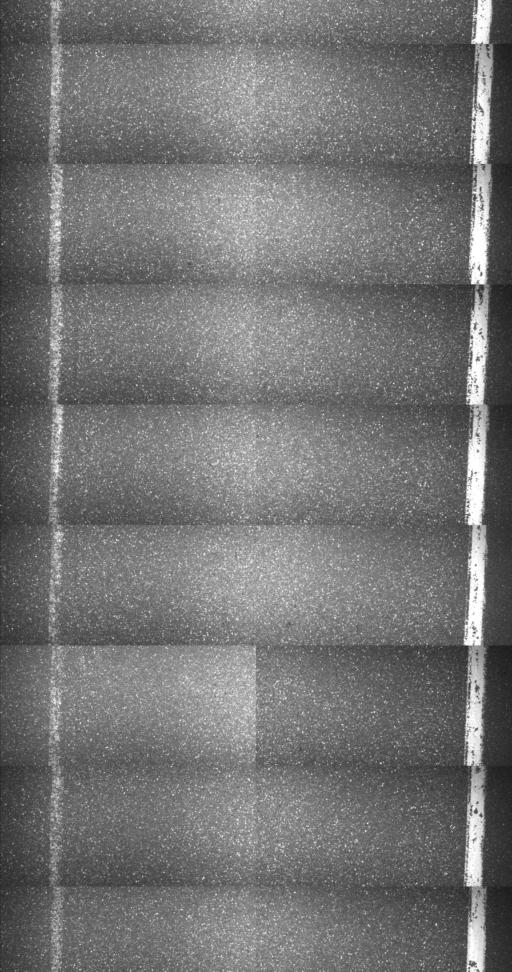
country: US
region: Vermont
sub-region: Washington County
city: Barre
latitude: 44.2764
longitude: -72.4798
